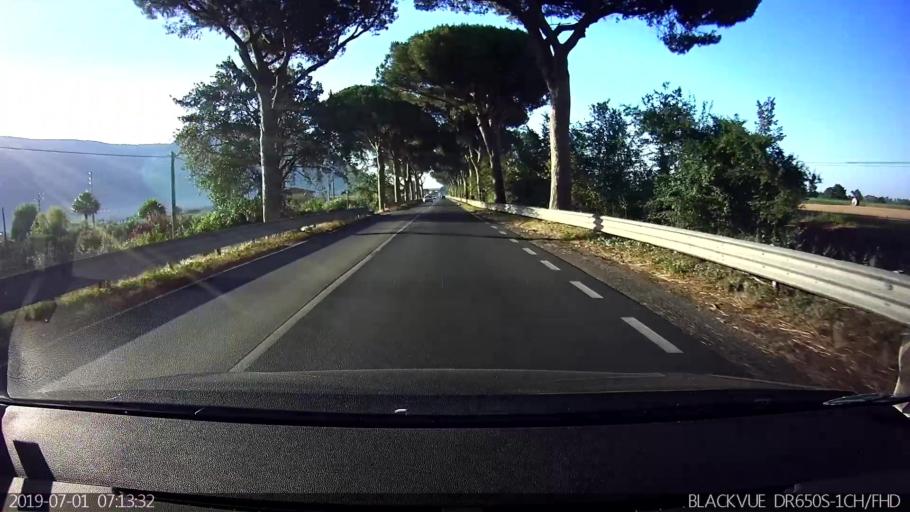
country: IT
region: Latium
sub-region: Provincia di Latina
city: Borgo Hermada
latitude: 41.3255
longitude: 13.1788
